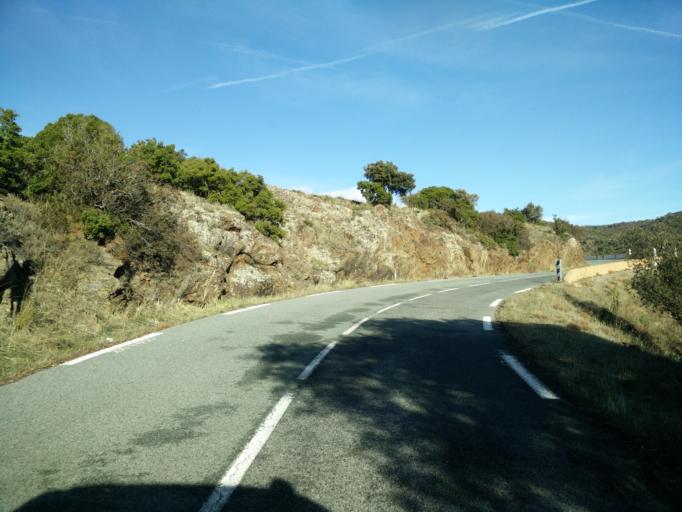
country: FR
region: Provence-Alpes-Cote d'Azur
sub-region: Departement du Var
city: Saint-Raphael
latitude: 43.4926
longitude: 6.7782
